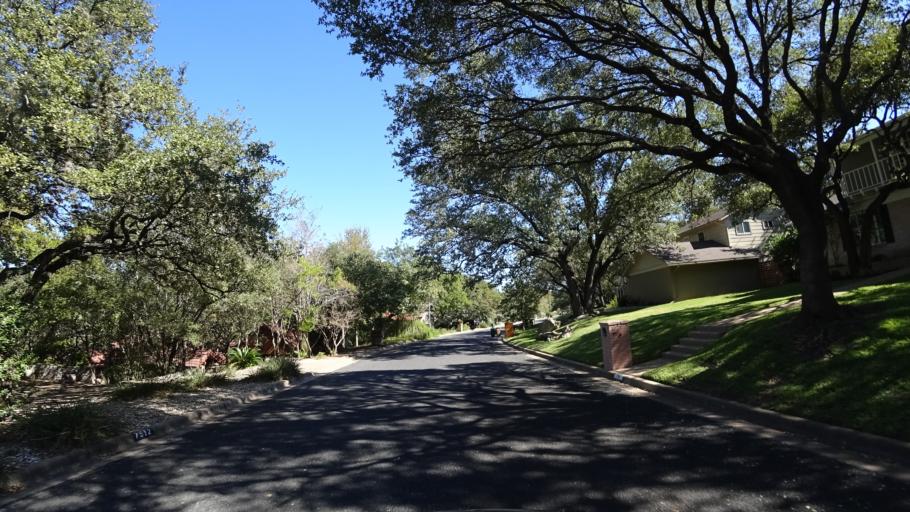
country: US
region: Texas
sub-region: Travis County
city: West Lake Hills
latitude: 30.3612
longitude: -97.7553
